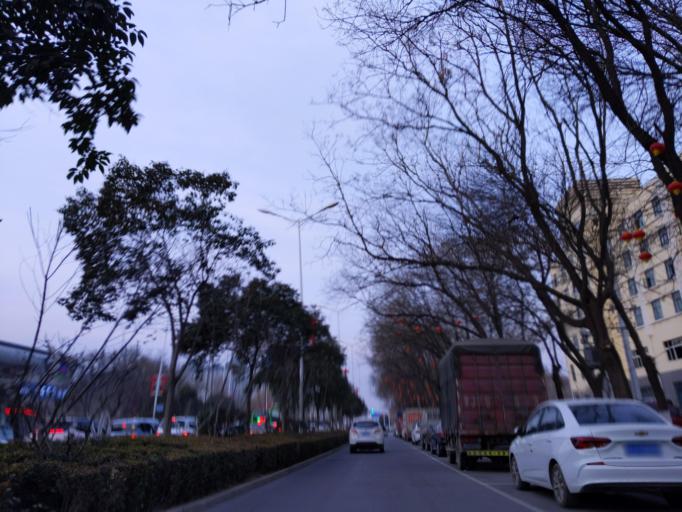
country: CN
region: Henan Sheng
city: Puyang
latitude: 35.7795
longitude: 115.0207
